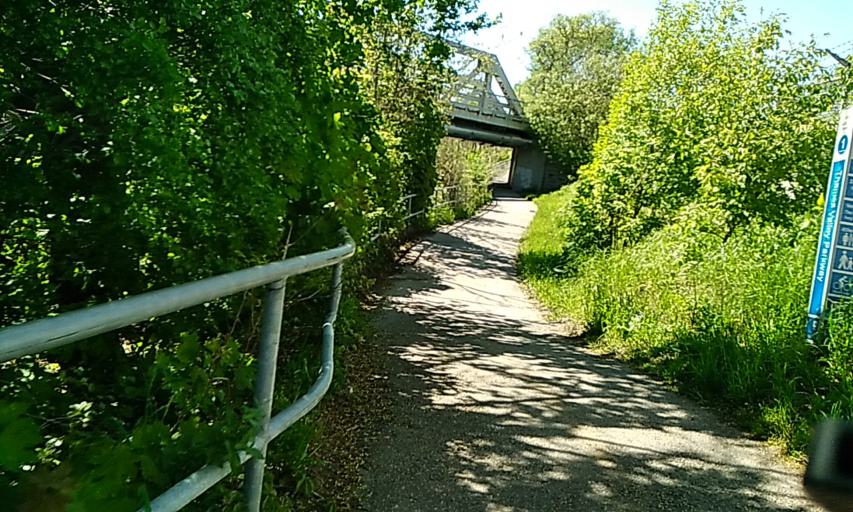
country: CA
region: Ontario
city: London
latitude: 42.9767
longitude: -81.2506
